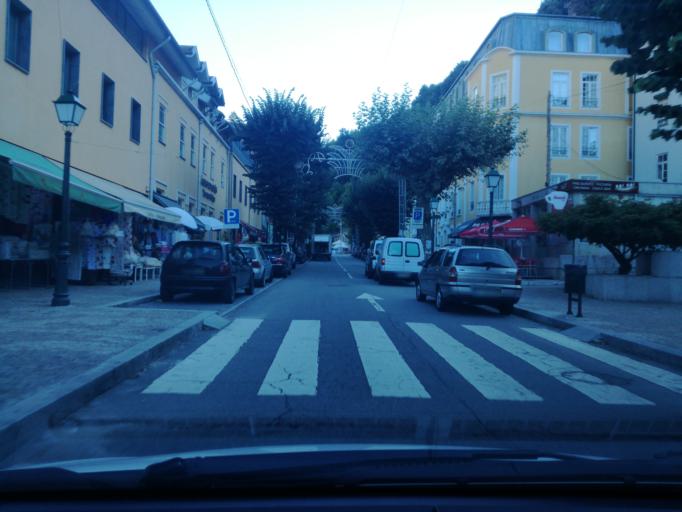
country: PT
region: Braga
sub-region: Vieira do Minho
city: Real
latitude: 41.7284
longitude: -8.1618
